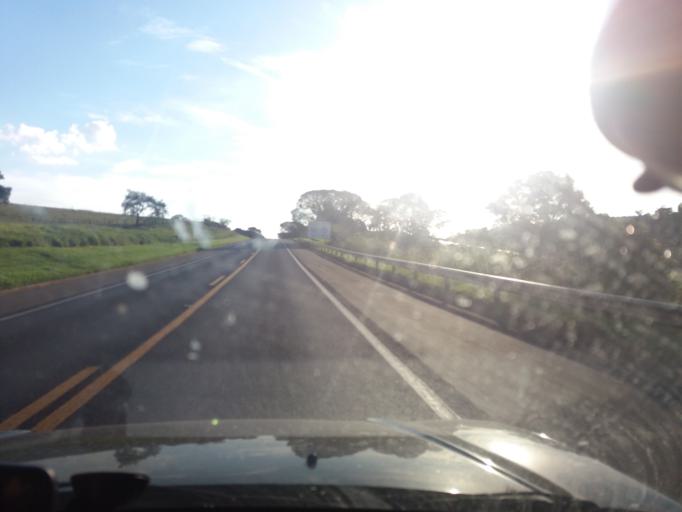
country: BR
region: Sao Paulo
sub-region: Buri
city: Buri
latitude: -23.9309
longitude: -48.6431
